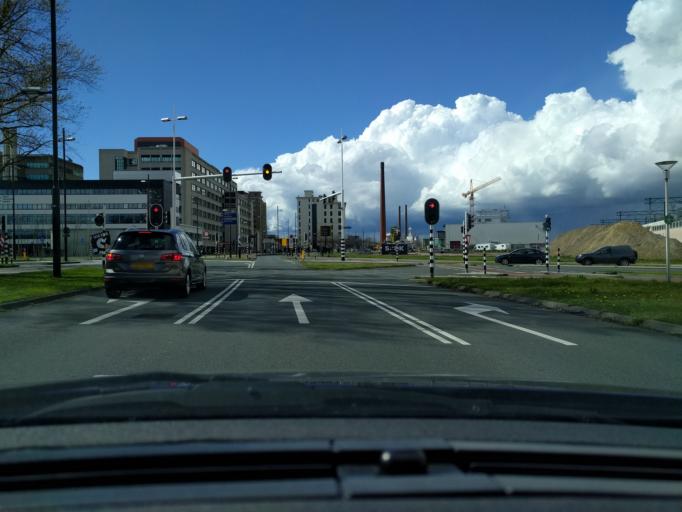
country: NL
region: North Brabant
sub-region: Gemeente Eindhoven
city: Eindhoven
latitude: 51.4449
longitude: 5.4637
